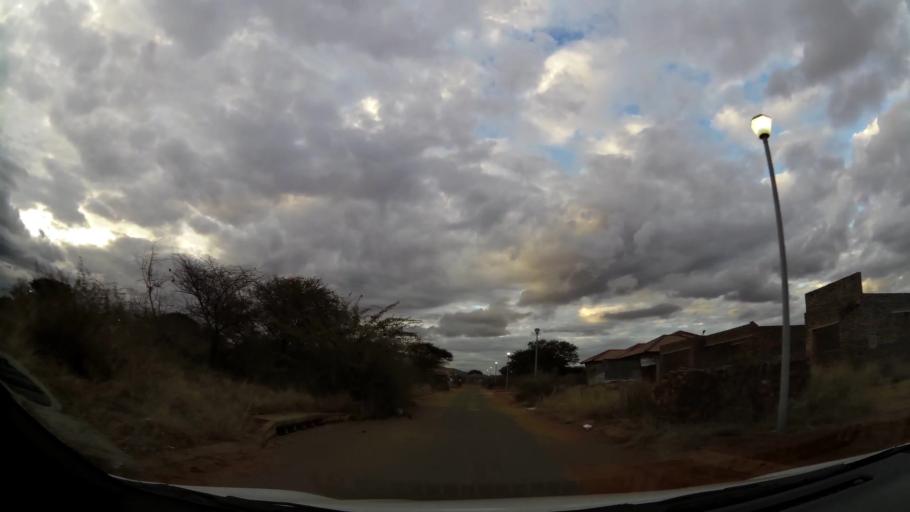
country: ZA
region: Limpopo
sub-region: Waterberg District Municipality
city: Mokopane
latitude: -24.2045
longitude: 28.9948
